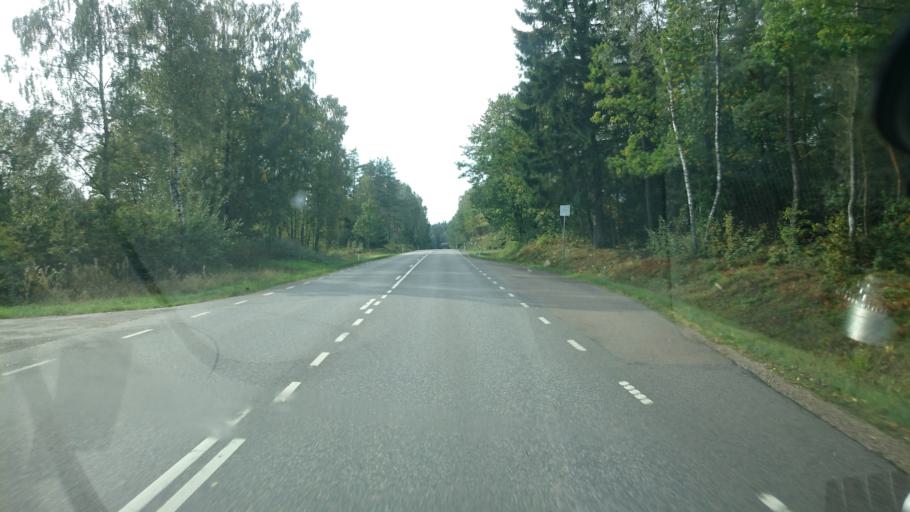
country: SE
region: Vaestra Goetaland
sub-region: Alingsas Kommun
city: Alingsas
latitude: 58.0130
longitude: 12.4497
